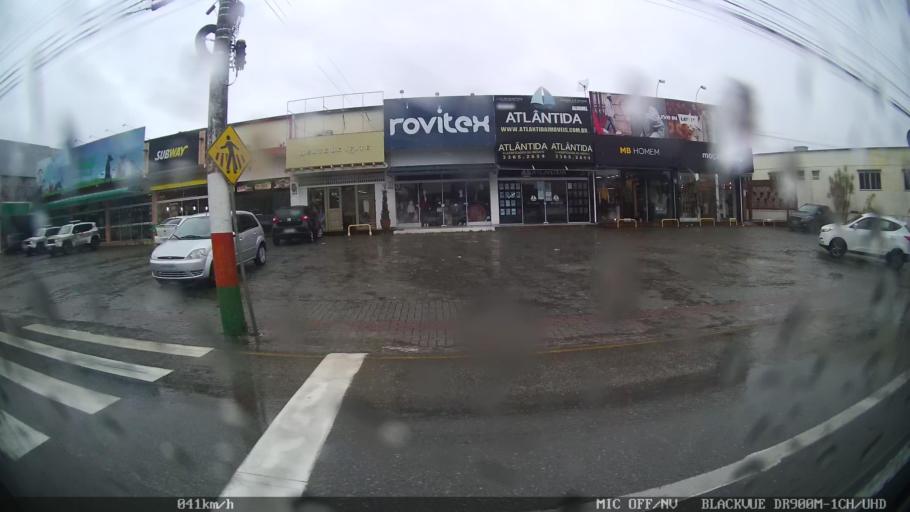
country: BR
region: Santa Catarina
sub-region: Balneario Camboriu
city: Balneario Camboriu
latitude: -27.0210
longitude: -48.6520
